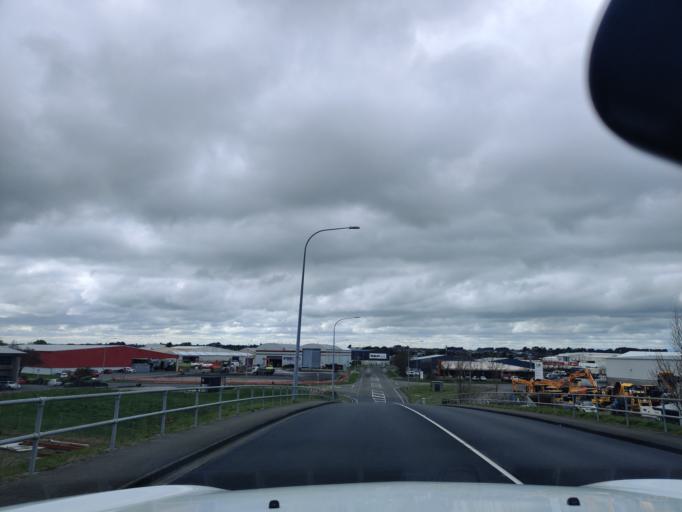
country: NZ
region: Manawatu-Wanganui
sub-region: Palmerston North City
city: Palmerston North
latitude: -40.3372
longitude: 175.6440
